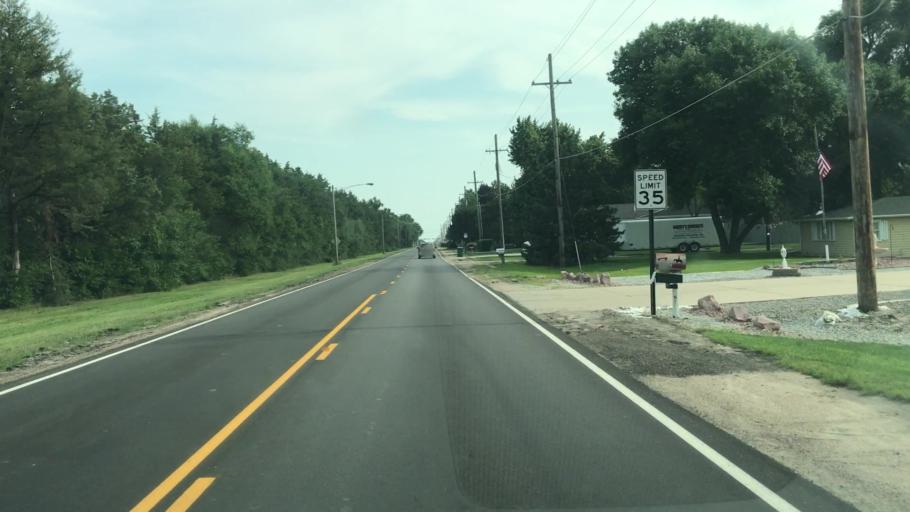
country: US
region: Nebraska
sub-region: Hall County
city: Grand Island
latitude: 40.9516
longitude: -98.3788
